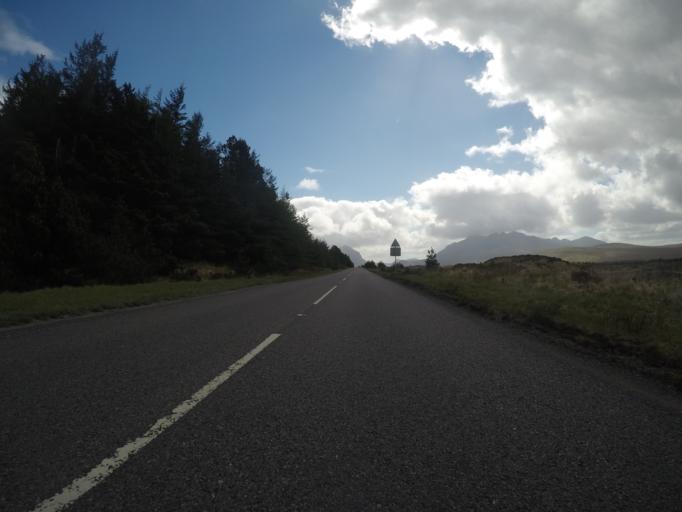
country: GB
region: Scotland
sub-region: Highland
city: Isle of Skye
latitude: 57.3184
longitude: -6.2030
